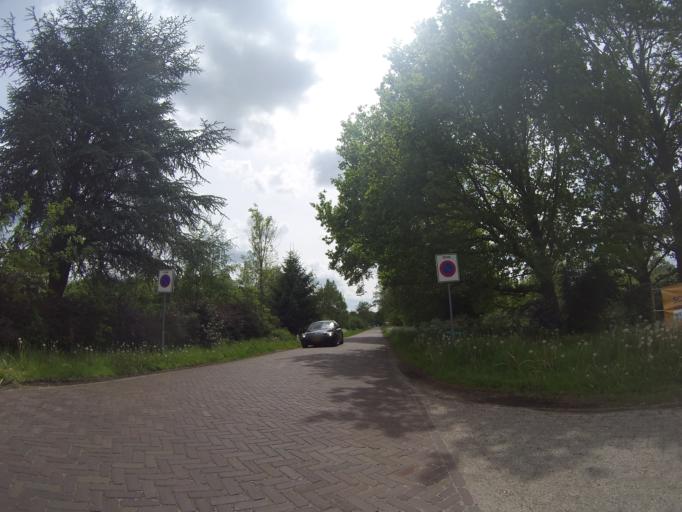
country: NL
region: Drenthe
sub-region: Gemeente Borger-Odoorn
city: Borger
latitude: 52.8482
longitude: 6.6653
